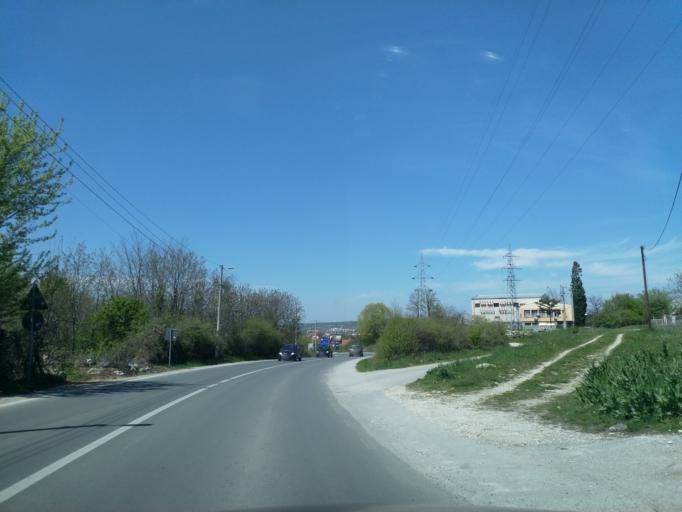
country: RS
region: Central Serbia
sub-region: Sumadijski Okrug
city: Arangelovac
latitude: 44.3169
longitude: 20.5425
